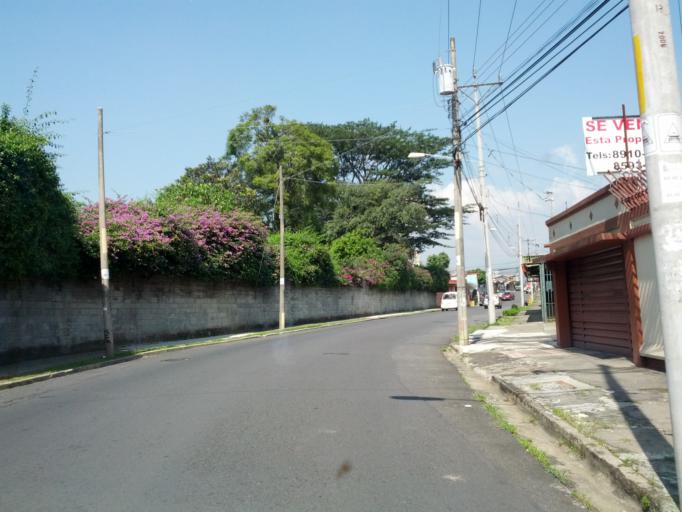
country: CR
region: Alajuela
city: Alajuela
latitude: 10.0142
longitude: -84.2073
